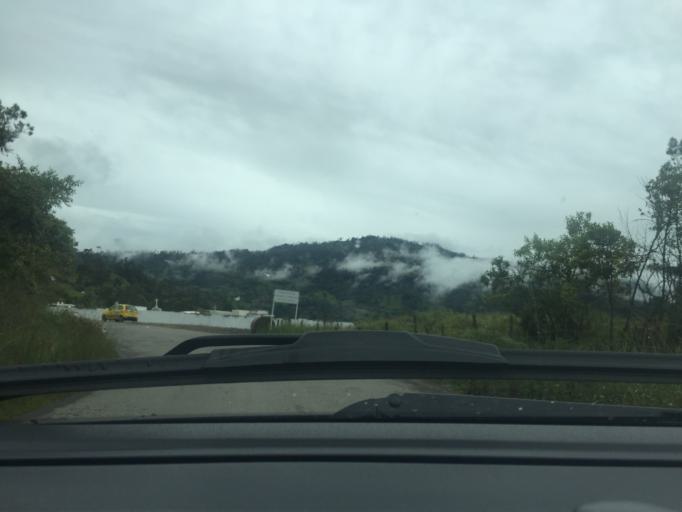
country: CO
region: Cundinamarca
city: Junin
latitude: 4.8095
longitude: -73.7066
